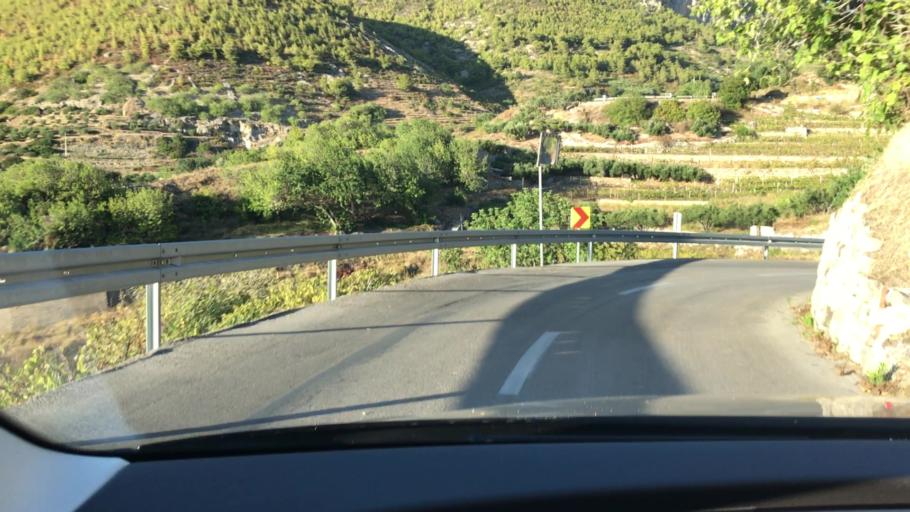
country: HR
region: Splitsko-Dalmatinska
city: Komiza
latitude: 43.0413
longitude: 16.0975
